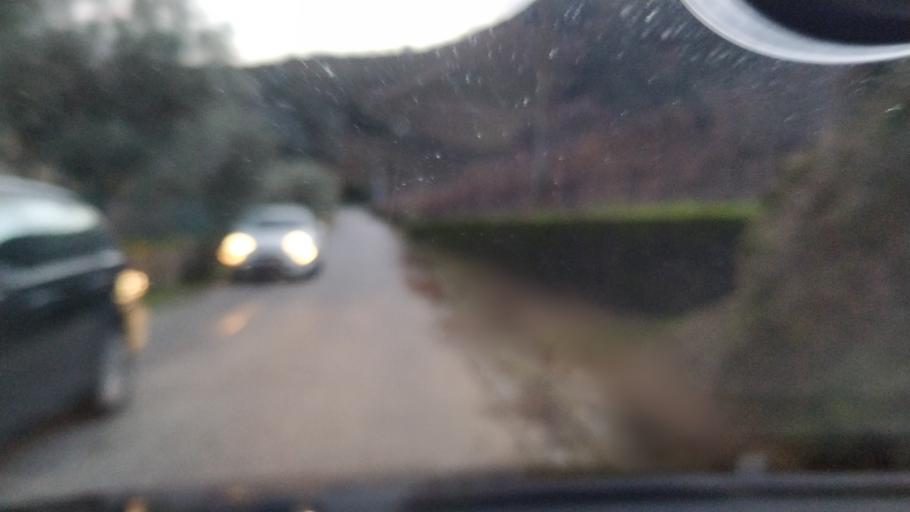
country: PT
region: Vila Real
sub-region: Santa Marta de Penaguiao
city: Santa Marta de Penaguiao
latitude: 41.2350
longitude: -7.7789
